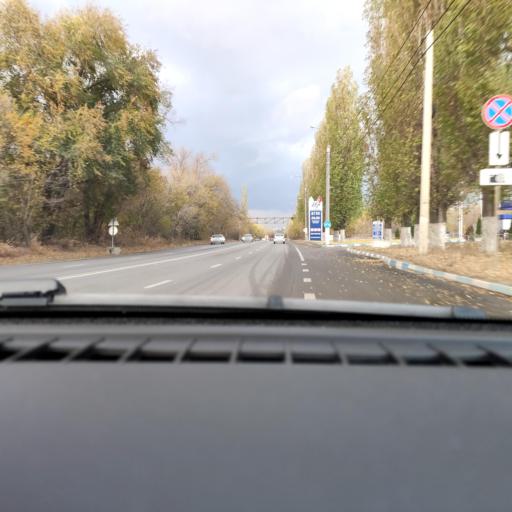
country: RU
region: Voronezj
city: Maslovka
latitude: 51.6014
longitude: 39.2534
